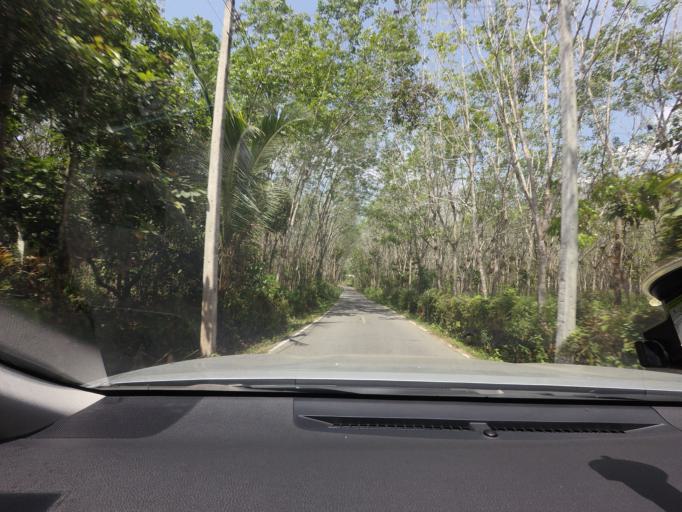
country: TH
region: Narathiwat
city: Rueso
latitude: 6.3790
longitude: 101.5039
